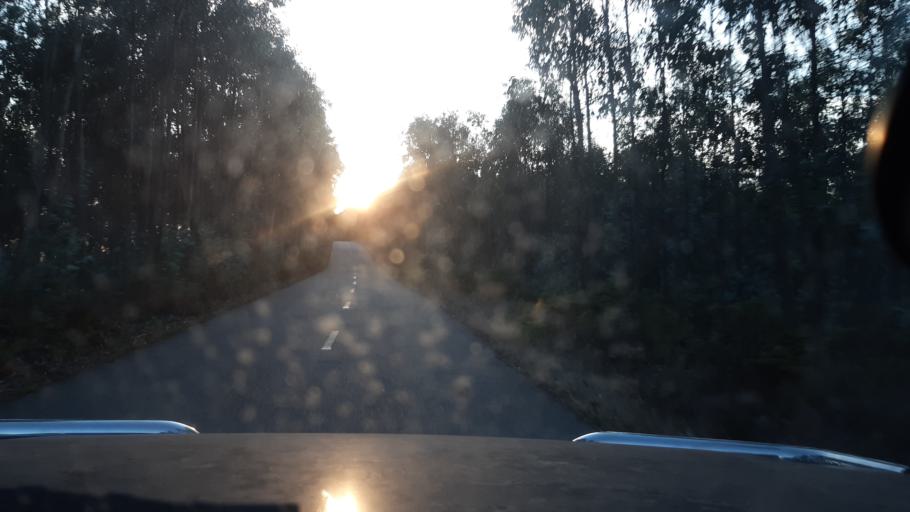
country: PT
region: Aveiro
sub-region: Agueda
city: Aguada de Cima
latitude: 40.5598
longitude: -8.2986
